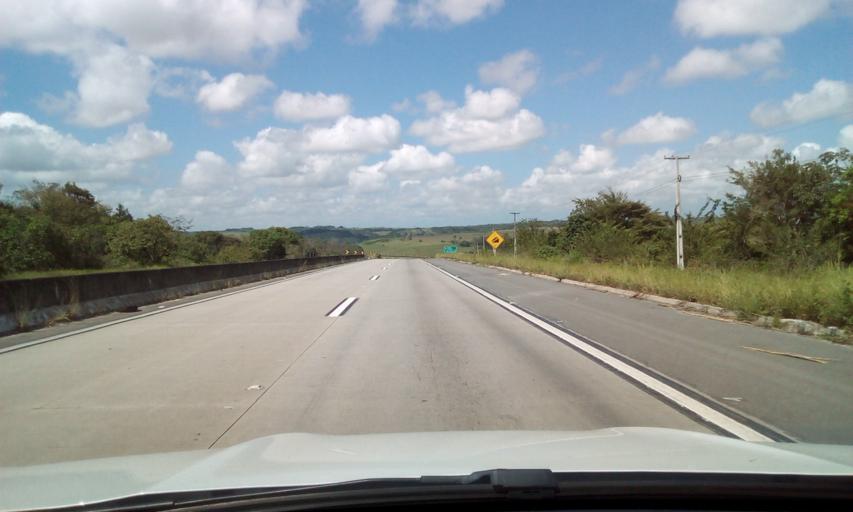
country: BR
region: Paraiba
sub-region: Alhandra
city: Alhandra
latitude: -7.4180
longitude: -34.9599
